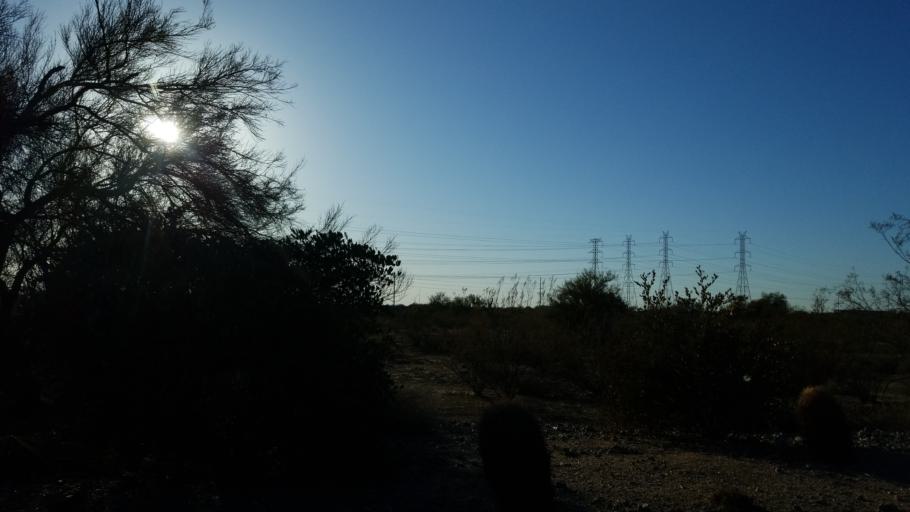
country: US
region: Arizona
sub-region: Maricopa County
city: Paradise Valley
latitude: 33.6482
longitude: -111.8853
